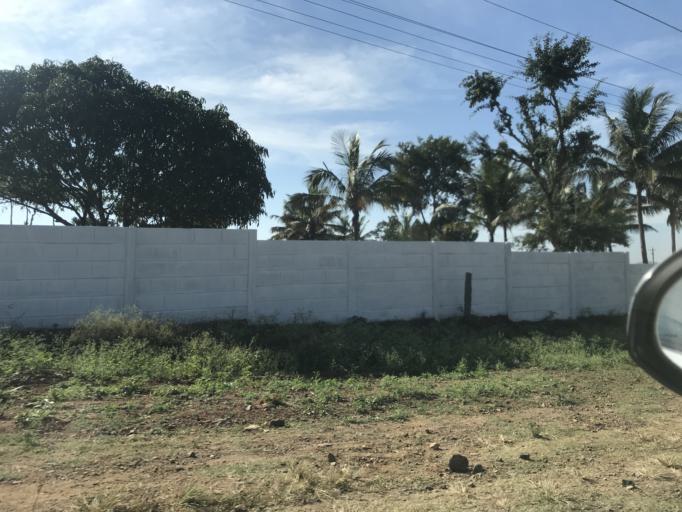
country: IN
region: Karnataka
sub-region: Mysore
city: Mysore
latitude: 12.2181
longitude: 76.5707
